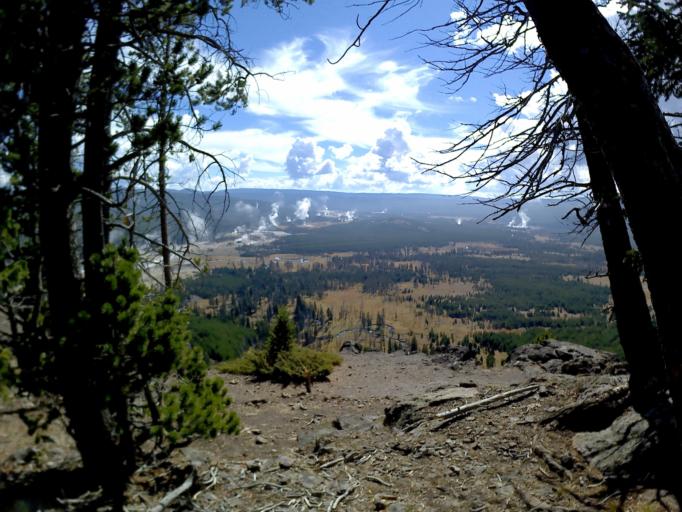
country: US
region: Montana
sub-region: Gallatin County
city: West Yellowstone
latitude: 44.4871
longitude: -110.8663
